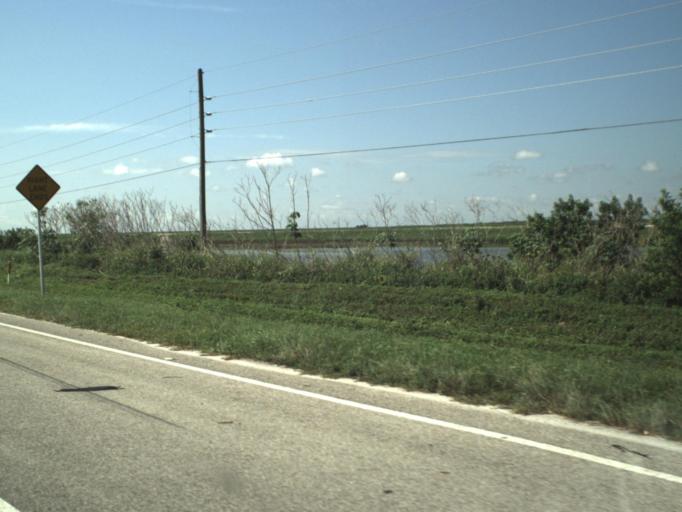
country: US
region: Florida
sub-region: Palm Beach County
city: Belle Glade Camp
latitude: 26.4141
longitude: -80.5993
